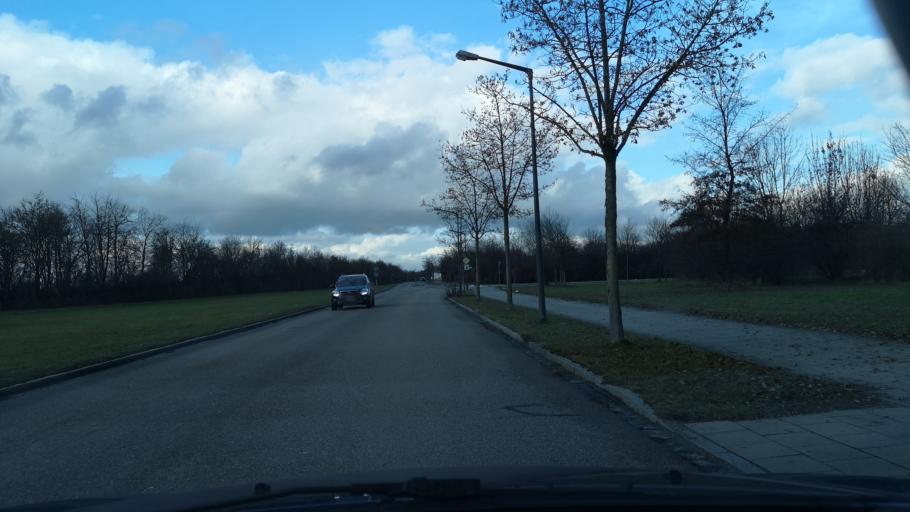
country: DE
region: Bavaria
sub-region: Upper Bavaria
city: Pliening
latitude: 48.1725
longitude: 11.7912
